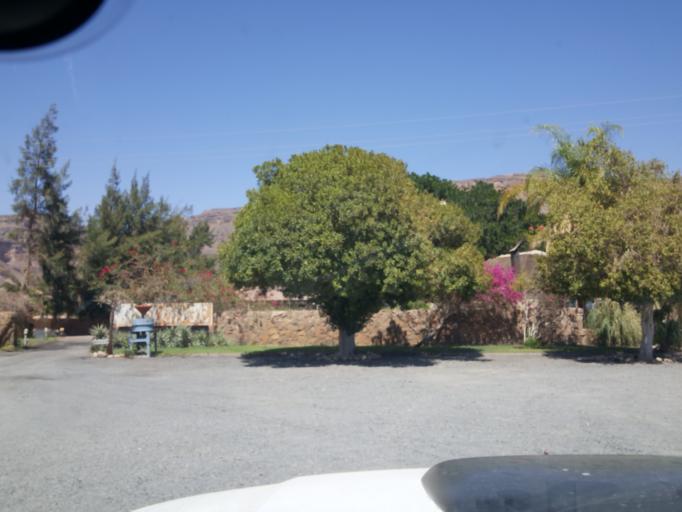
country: ZA
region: Northern Cape
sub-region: Namakwa District Municipality
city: Port Nolloth
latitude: -28.7437
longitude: 17.6175
